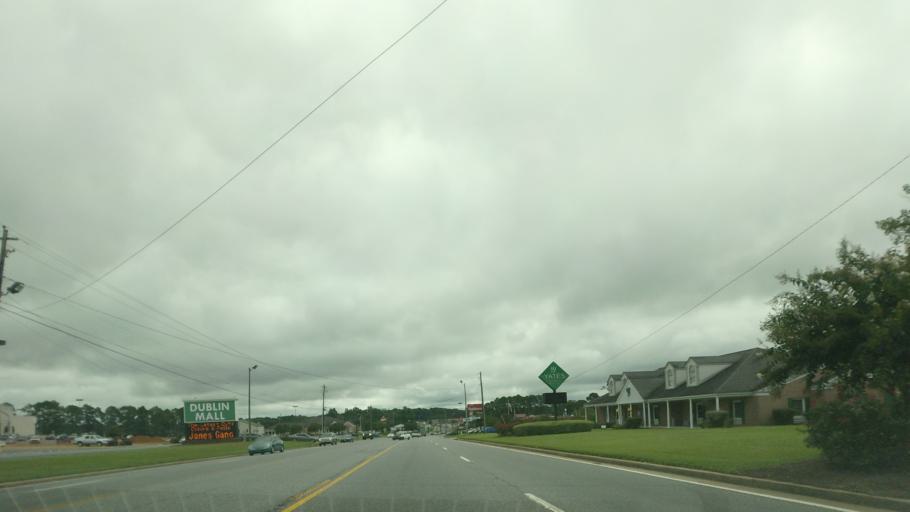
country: US
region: Georgia
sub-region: Laurens County
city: Dublin
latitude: 32.5414
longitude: -82.9507
